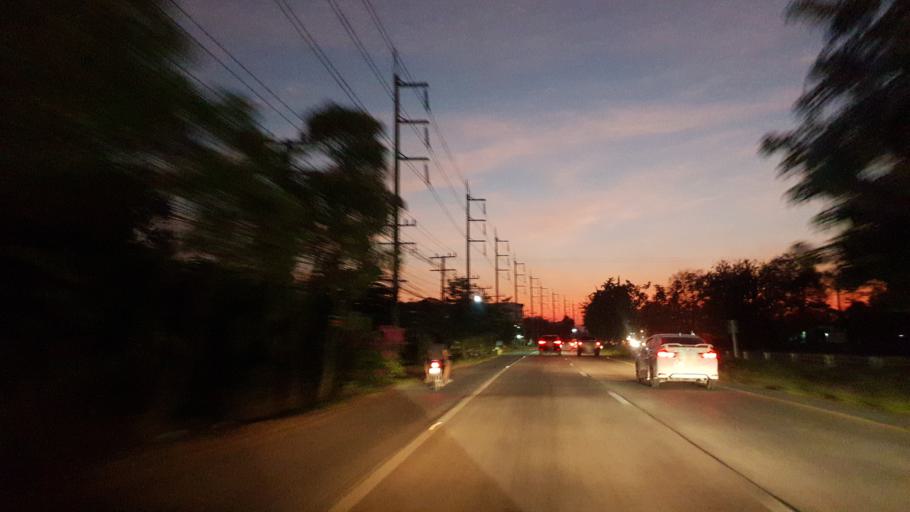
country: TH
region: Phitsanulok
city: Wang Thong
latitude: 16.8246
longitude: 100.3545
